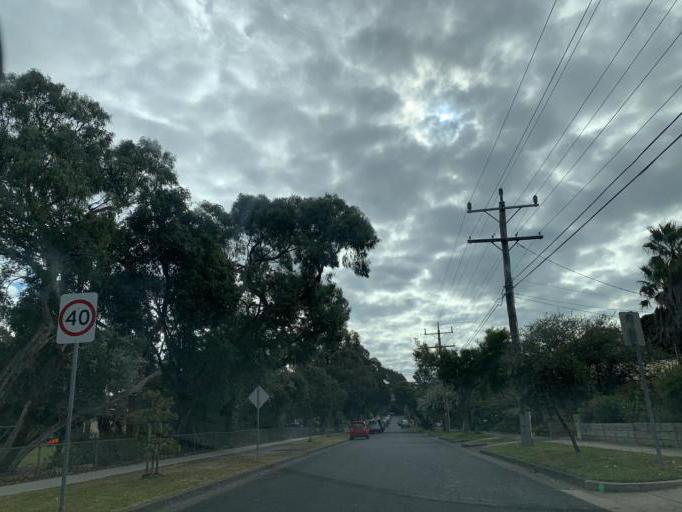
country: AU
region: Victoria
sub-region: Bayside
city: Cheltenham
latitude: -37.9737
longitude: 145.0388
